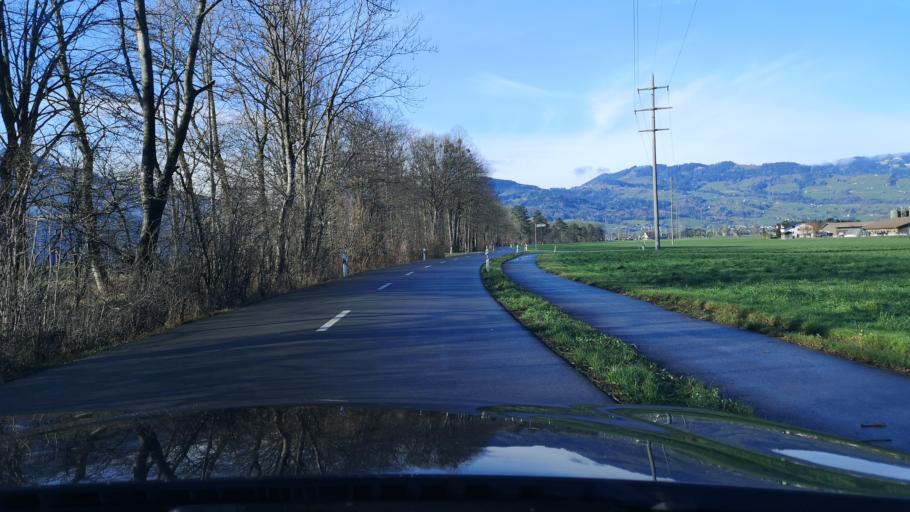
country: CH
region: Saint Gallen
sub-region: Wahlkreis Rheintal
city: Oberriet
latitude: 47.3402
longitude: 9.5766
